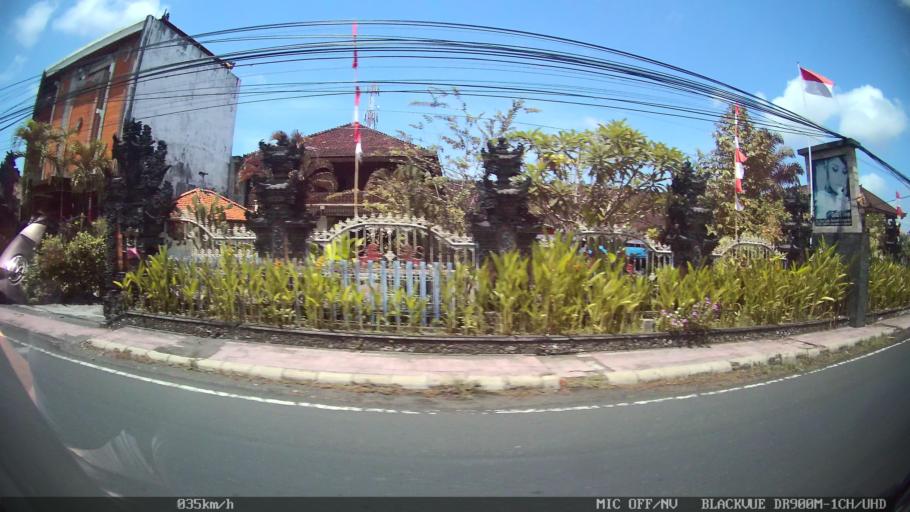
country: ID
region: Bali
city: Banjar Jabejero
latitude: -8.6041
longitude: 115.2580
